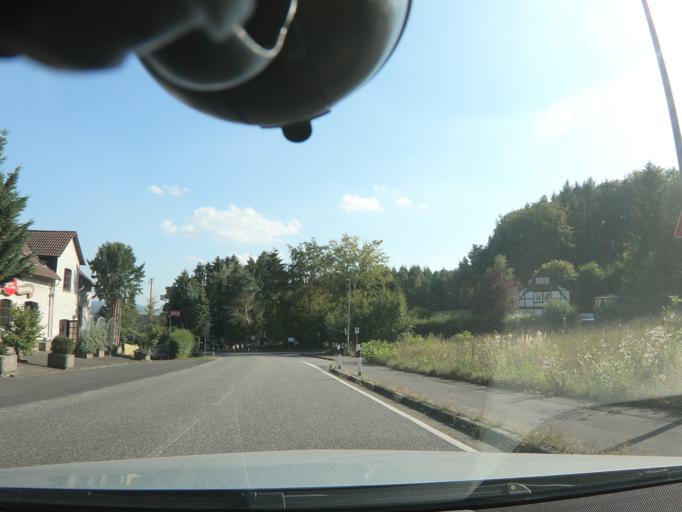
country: DE
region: Hesse
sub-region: Regierungsbezirk Giessen
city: Marburg an der Lahn
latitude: 50.7914
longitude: 8.8174
